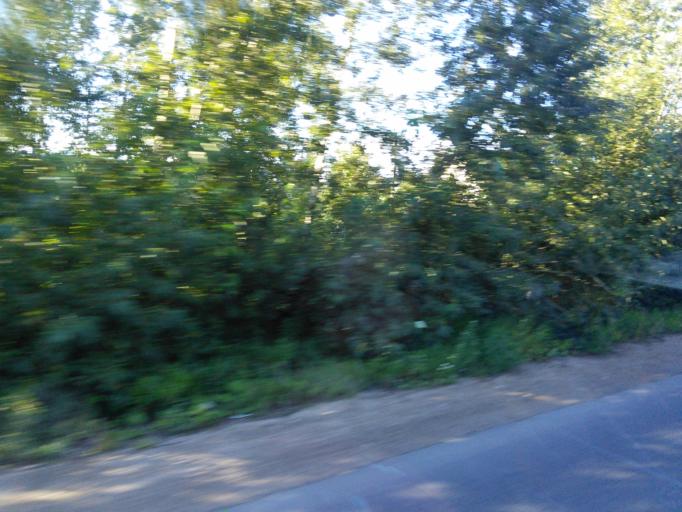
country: RU
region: Jaroslavl
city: Poshekhon'ye
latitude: 58.4937
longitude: 39.0925
